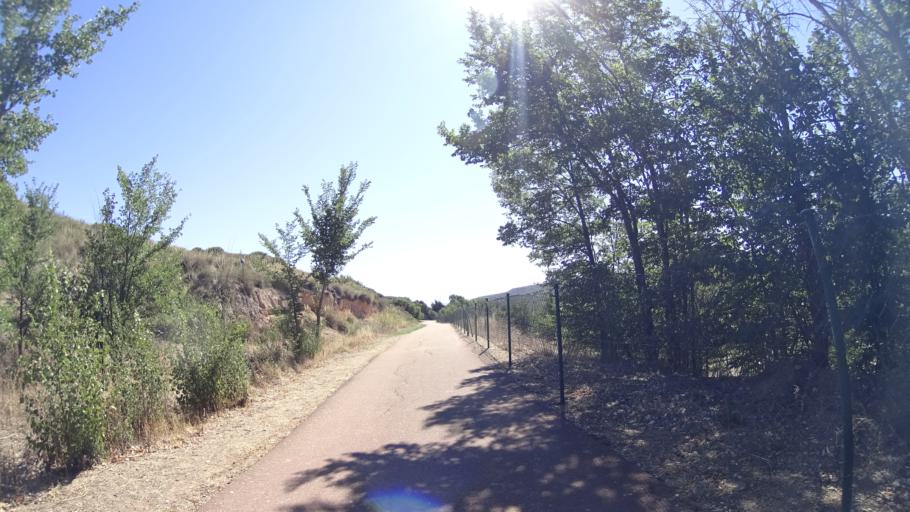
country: ES
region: Madrid
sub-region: Provincia de Madrid
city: Morata de Tajuna
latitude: 40.2309
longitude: -3.4038
